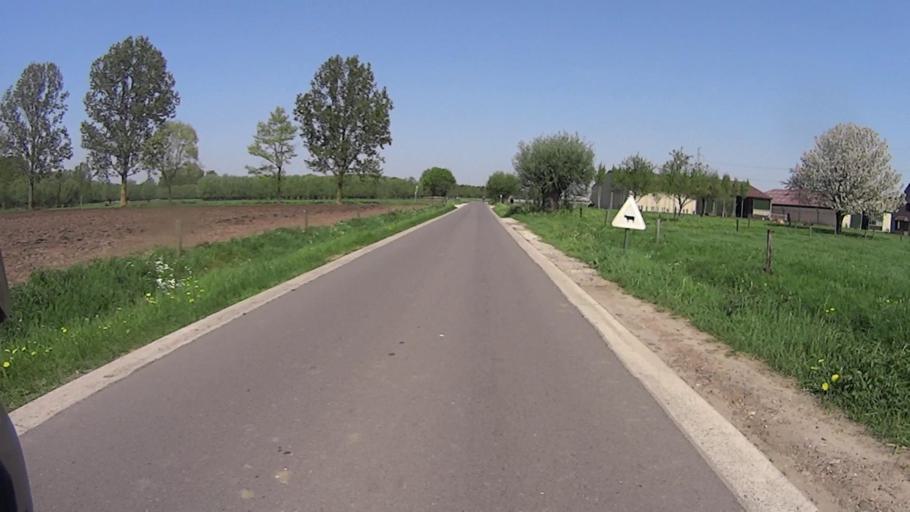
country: BE
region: Flanders
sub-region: Provincie Antwerpen
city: Sint-Amands
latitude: 51.0642
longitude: 4.2157
